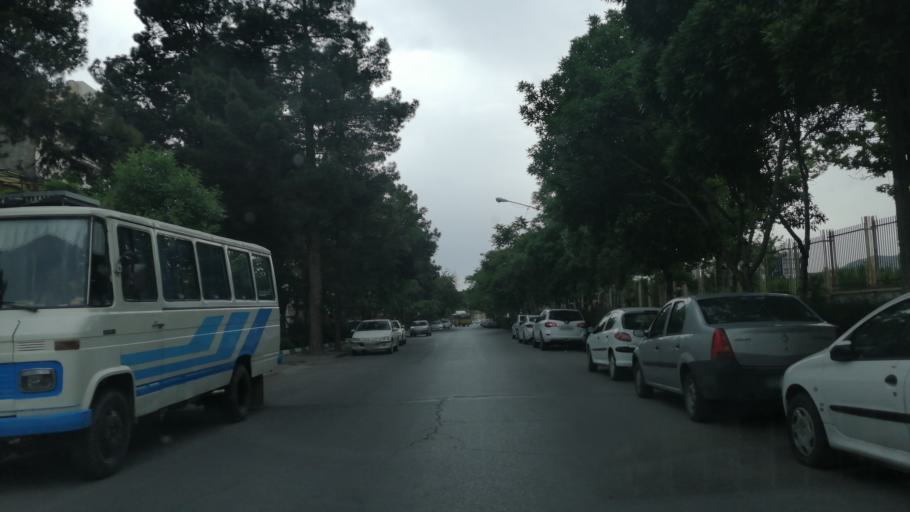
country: IR
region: Razavi Khorasan
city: Mashhad
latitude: 36.2879
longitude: 59.5815
